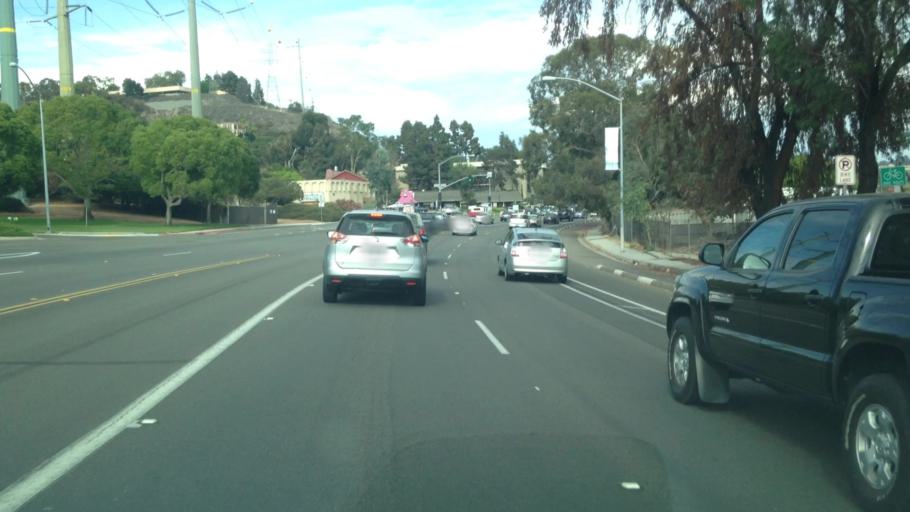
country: US
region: California
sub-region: San Diego County
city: San Diego
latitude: 32.7662
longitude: -117.1855
